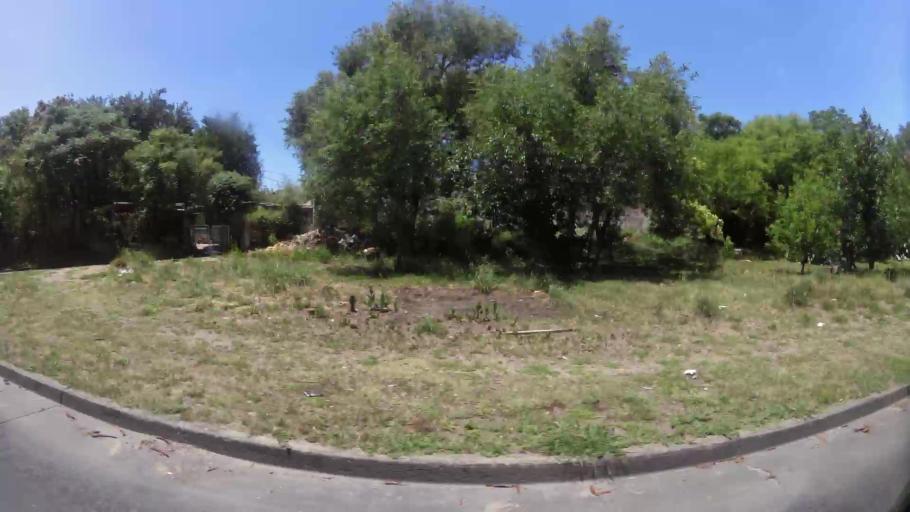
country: AR
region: Cordoba
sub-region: Departamento de Capital
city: Cordoba
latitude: -31.3999
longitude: -64.2037
